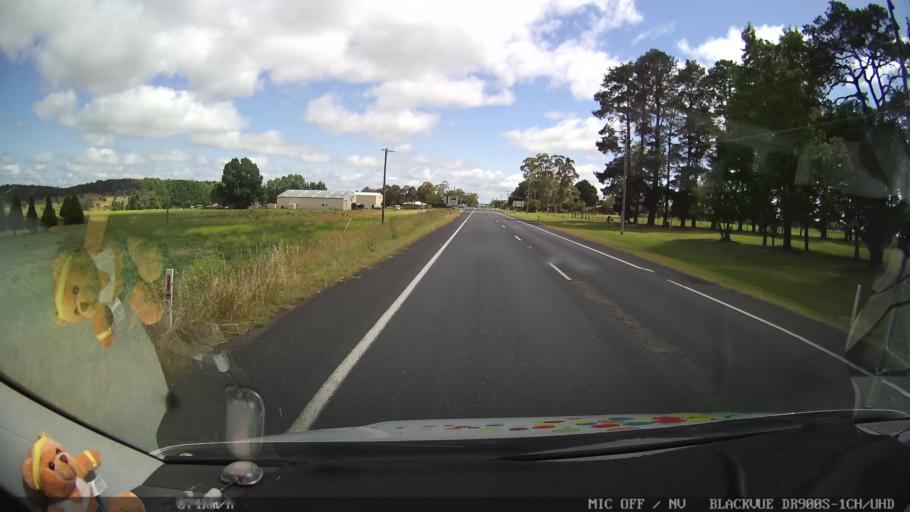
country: AU
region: New South Wales
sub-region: Glen Innes Severn
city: Glen Innes
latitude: -29.7677
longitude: 151.7325
